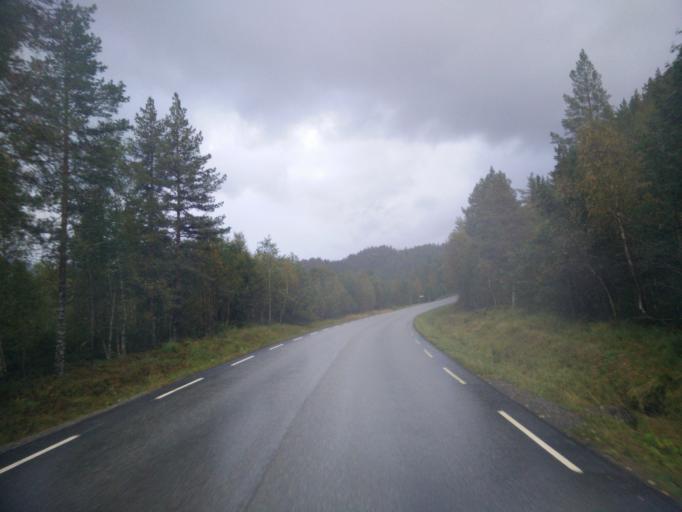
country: NO
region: More og Romsdal
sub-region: Surnadal
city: Surnadal
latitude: 63.0261
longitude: 8.6294
